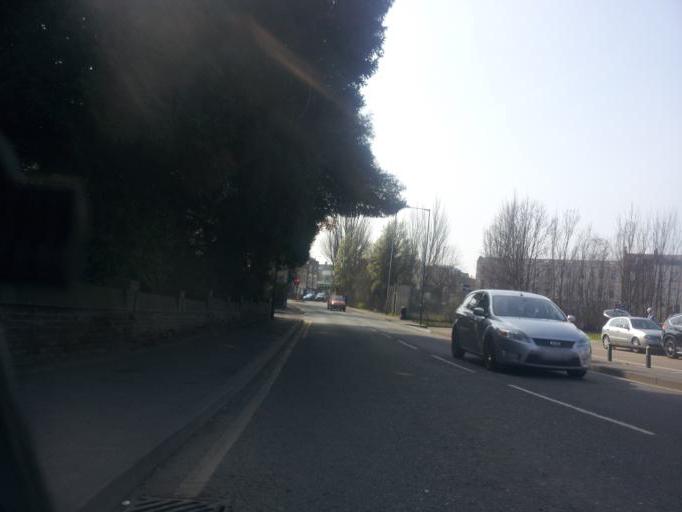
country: GB
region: England
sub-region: Kent
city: Gravesend
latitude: 51.4415
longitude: 0.3772
